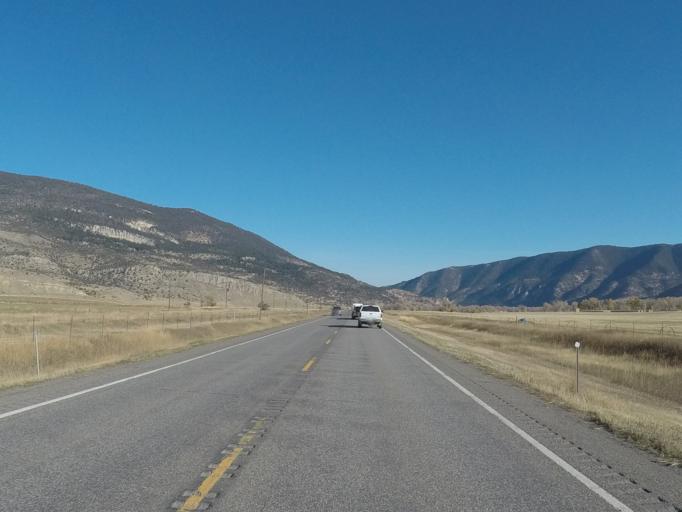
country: US
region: Montana
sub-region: Park County
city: Livingston
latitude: 45.5558
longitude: -110.5952
